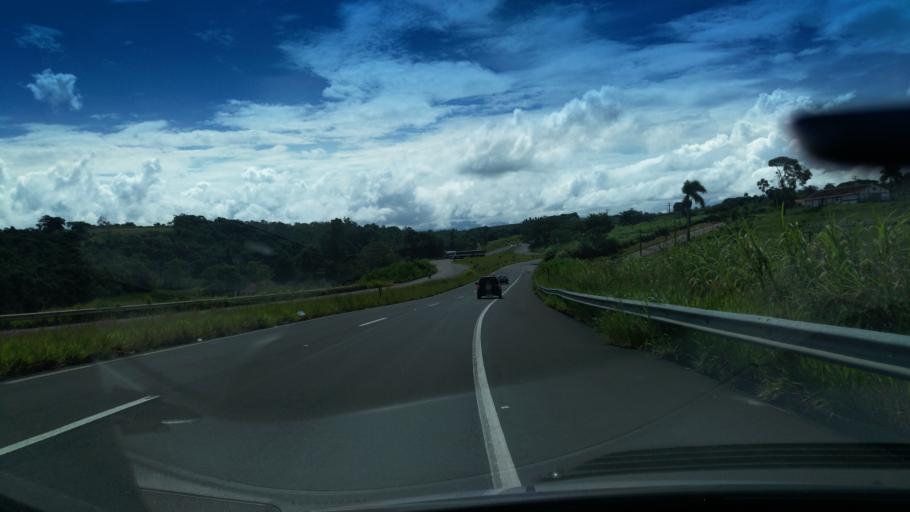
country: BR
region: Sao Paulo
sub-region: Santo Antonio Do Jardim
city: Espirito Santo do Pinhal
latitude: -22.1672
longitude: -46.7391
